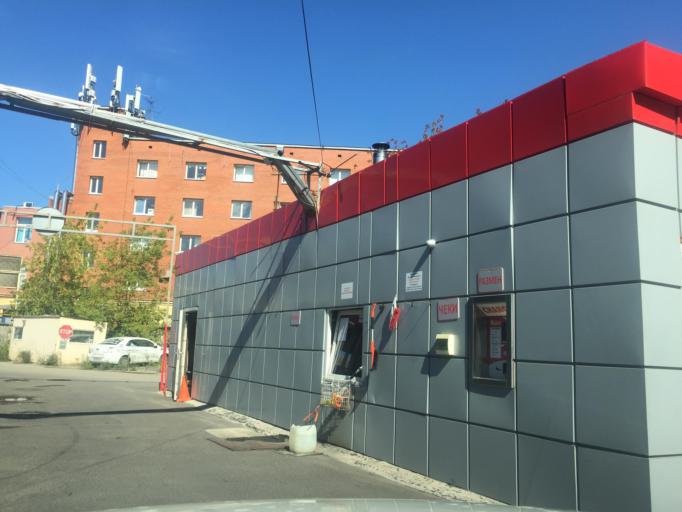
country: RU
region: St.-Petersburg
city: Kushelevka
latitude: 59.9918
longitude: 30.3576
